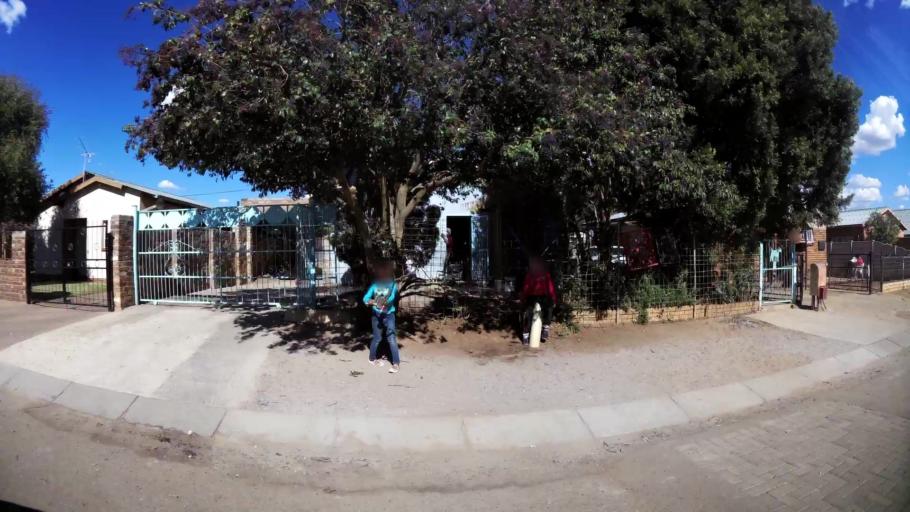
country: ZA
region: North-West
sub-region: Dr Kenneth Kaunda District Municipality
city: Klerksdorp
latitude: -26.8697
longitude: 26.5867
